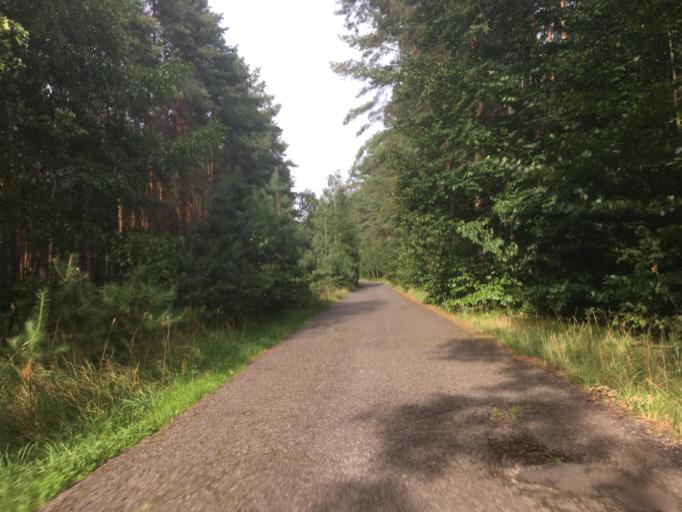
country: DE
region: Brandenburg
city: Melchow
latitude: 52.8004
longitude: 13.6928
